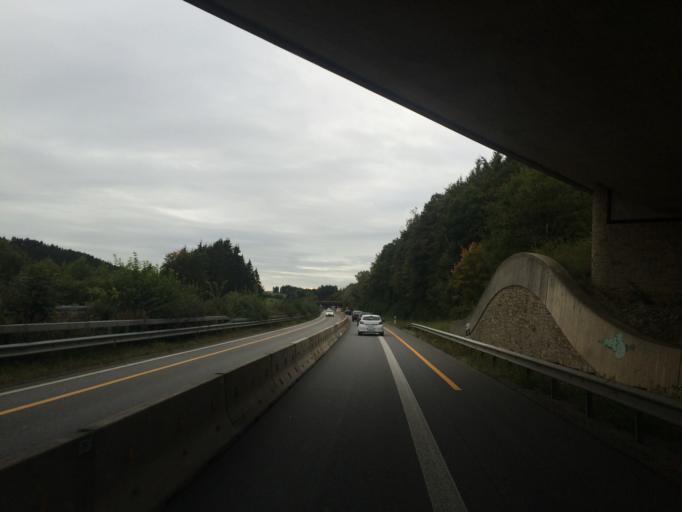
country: DE
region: Rheinland-Pfalz
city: Steiningen
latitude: 50.1855
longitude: 6.9026
